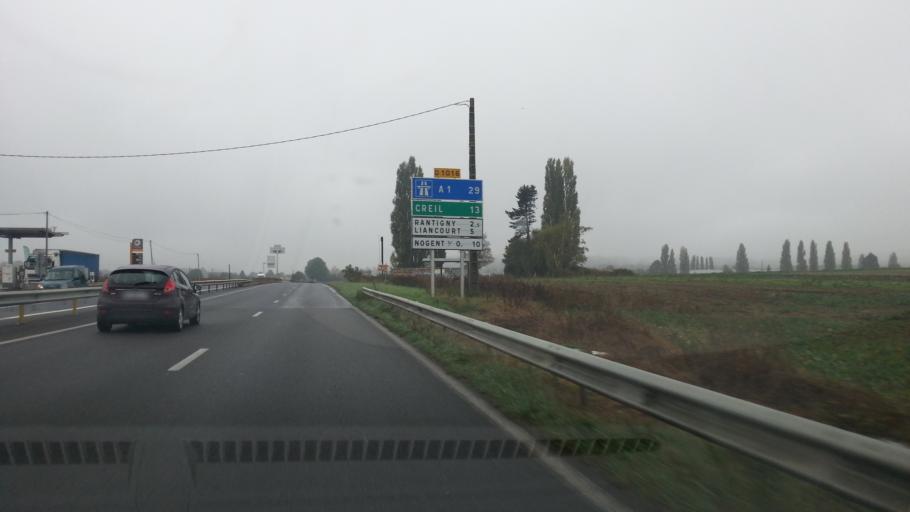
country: FR
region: Picardie
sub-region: Departement de l'Oise
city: Breuil-le-Vert
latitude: 49.3454
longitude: 2.4313
